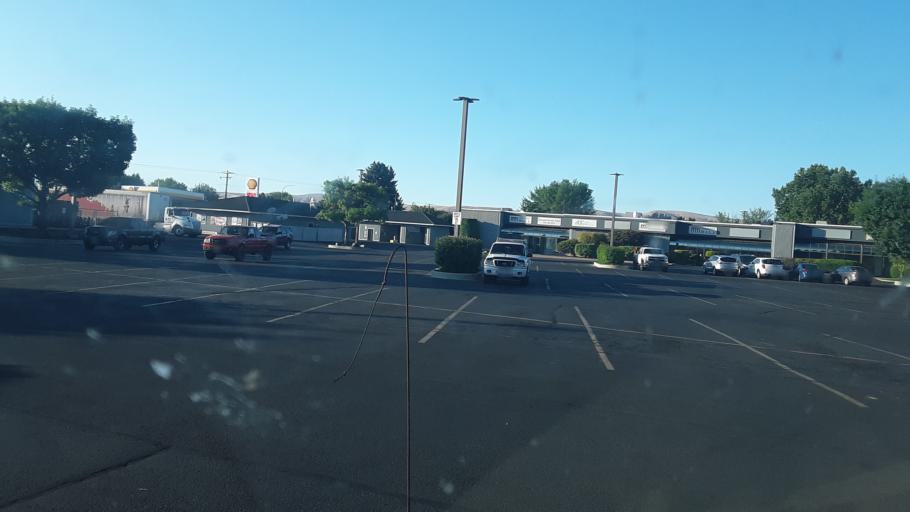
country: US
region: Washington
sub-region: Yakima County
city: West Valley
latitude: 46.5853
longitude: -120.6058
